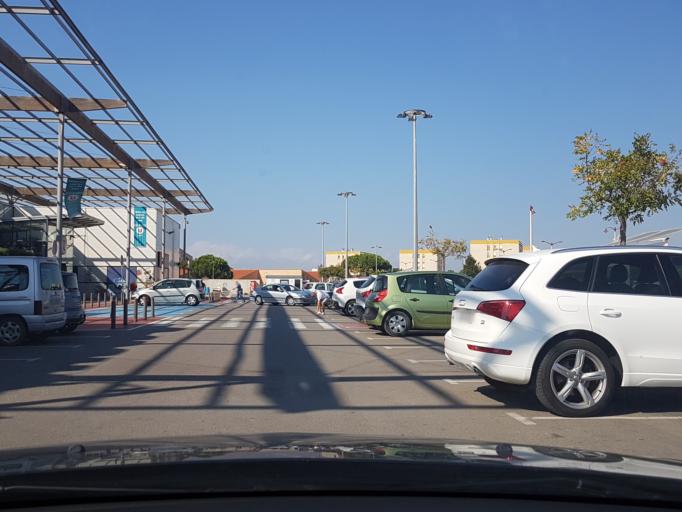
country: FR
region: Languedoc-Roussillon
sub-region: Departement de l'Aude
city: Port-la-Nouvelle
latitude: 43.0153
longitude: 3.0494
